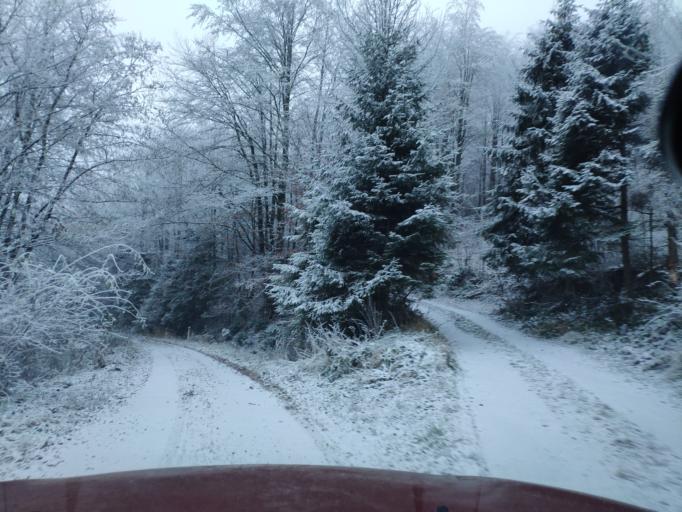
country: SK
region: Kosicky
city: Dobsina
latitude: 48.8108
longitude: 20.4852
